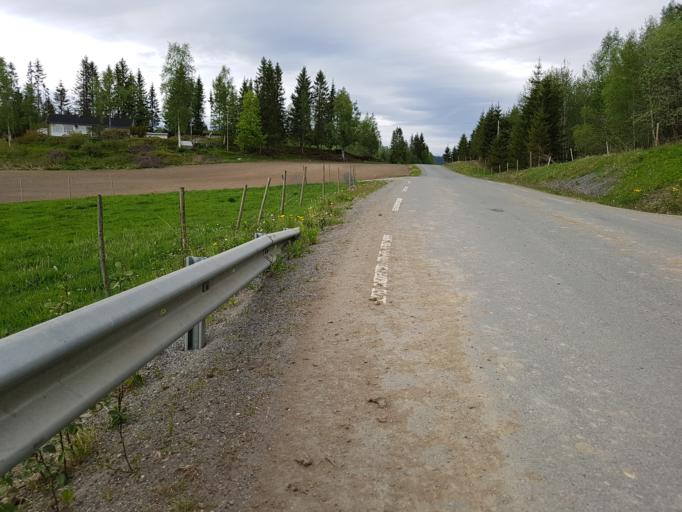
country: NO
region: Nord-Trondelag
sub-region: Levanger
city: Skogn
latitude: 63.6265
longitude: 11.2741
